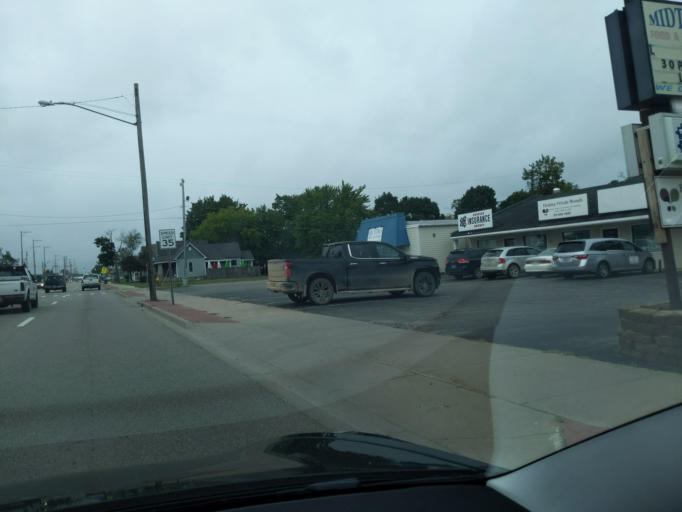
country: US
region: Michigan
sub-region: Wexford County
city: Cadillac
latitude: 44.2590
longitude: -85.4050
